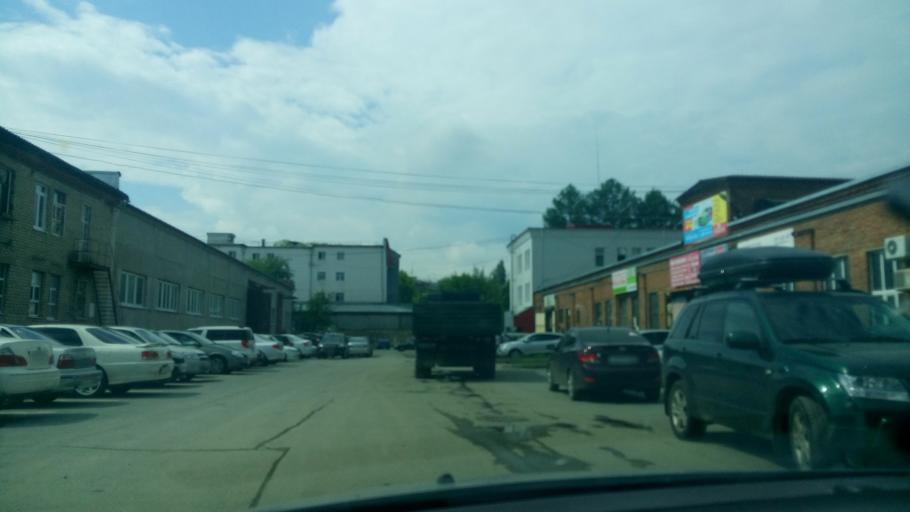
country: RU
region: Sverdlovsk
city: Yekaterinburg
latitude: 56.8573
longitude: 60.6614
